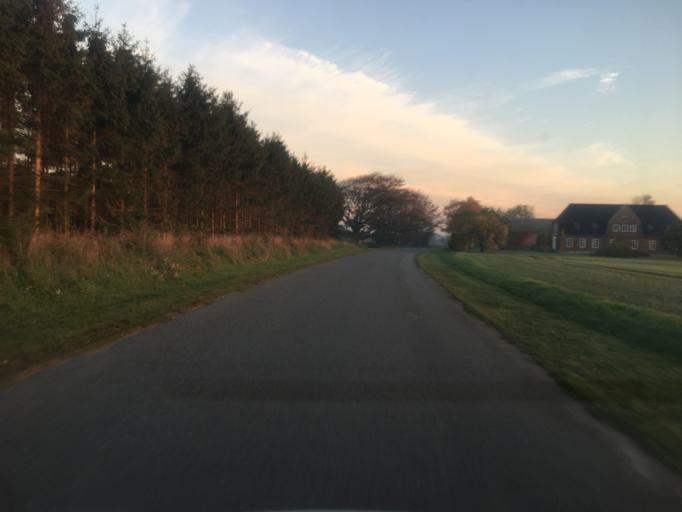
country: DK
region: South Denmark
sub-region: Tonder Kommune
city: Logumkloster
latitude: 55.0208
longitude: 9.0452
